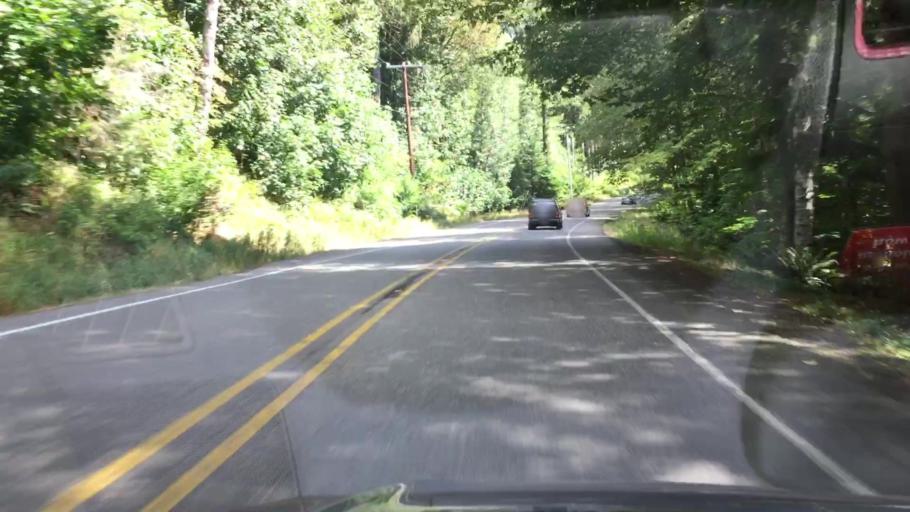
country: US
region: Washington
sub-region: Pierce County
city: Eatonville
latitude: 46.7544
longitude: -121.9455
